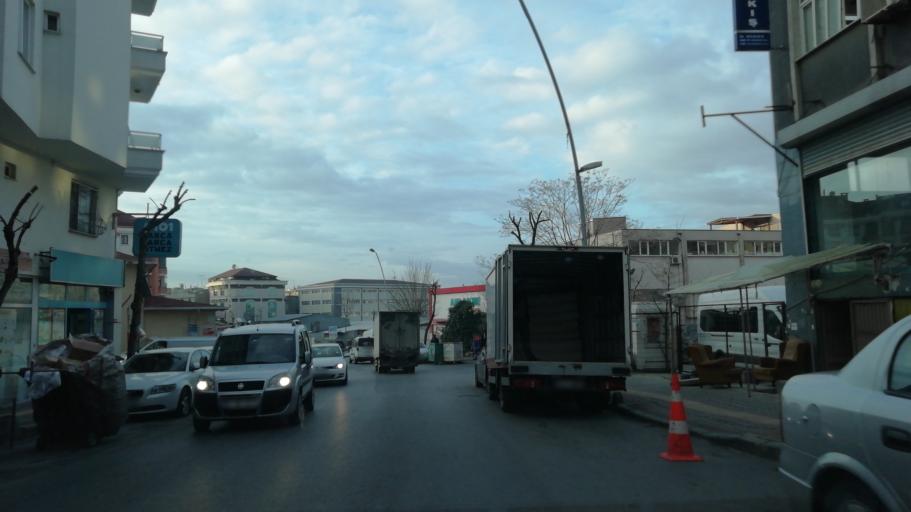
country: TR
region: Istanbul
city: Bahcelievler
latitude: 41.0046
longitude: 28.8268
